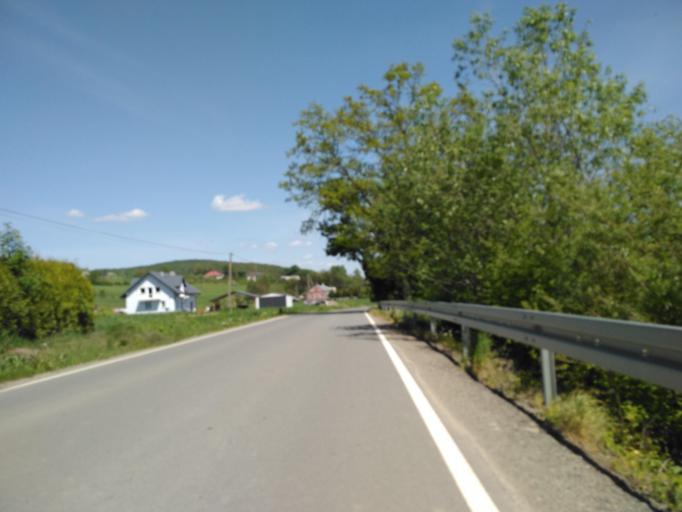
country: PL
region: Subcarpathian Voivodeship
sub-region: Powiat krosnienski
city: Dukla
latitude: 49.5948
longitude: 21.7004
